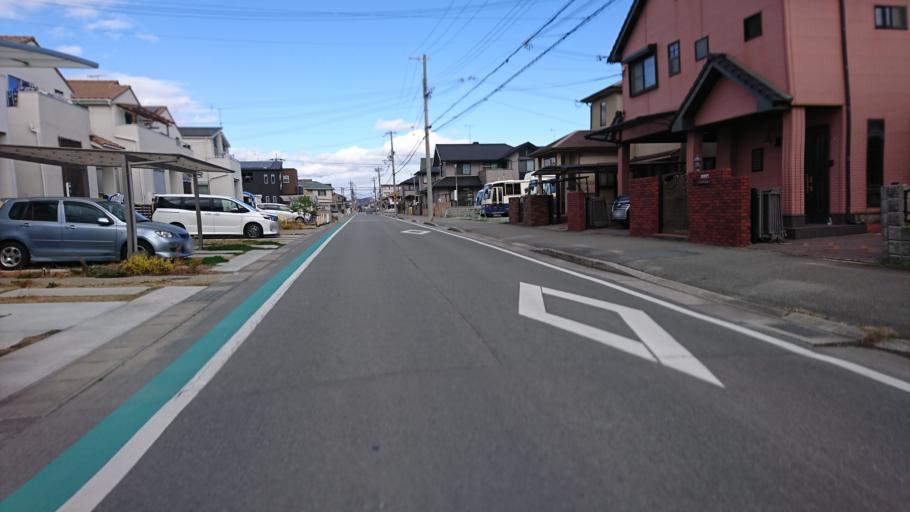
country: JP
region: Hyogo
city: Kakogawacho-honmachi
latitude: 34.7777
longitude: 134.8016
